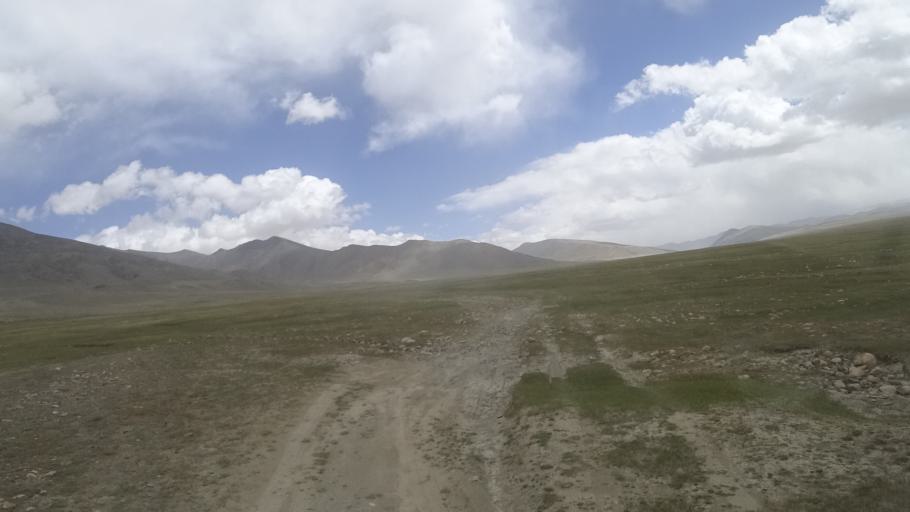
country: TJ
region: Gorno-Badakhshan
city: Murghob
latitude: 37.4858
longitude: 73.9887
